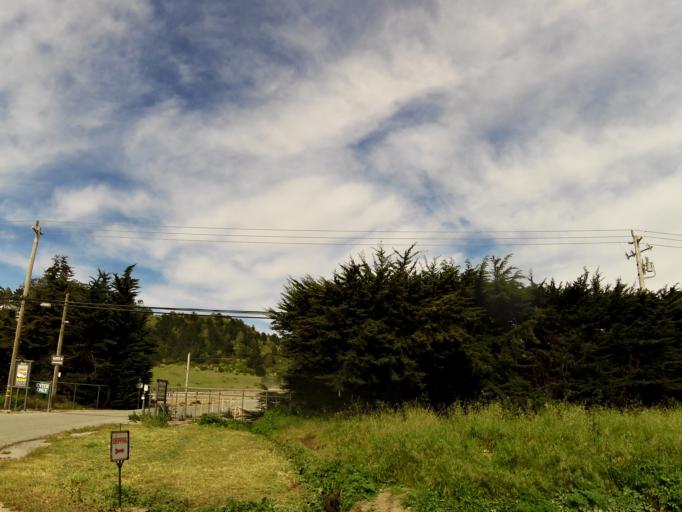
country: US
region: California
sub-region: San Mateo County
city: El Granada
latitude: 37.4921
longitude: -122.4524
